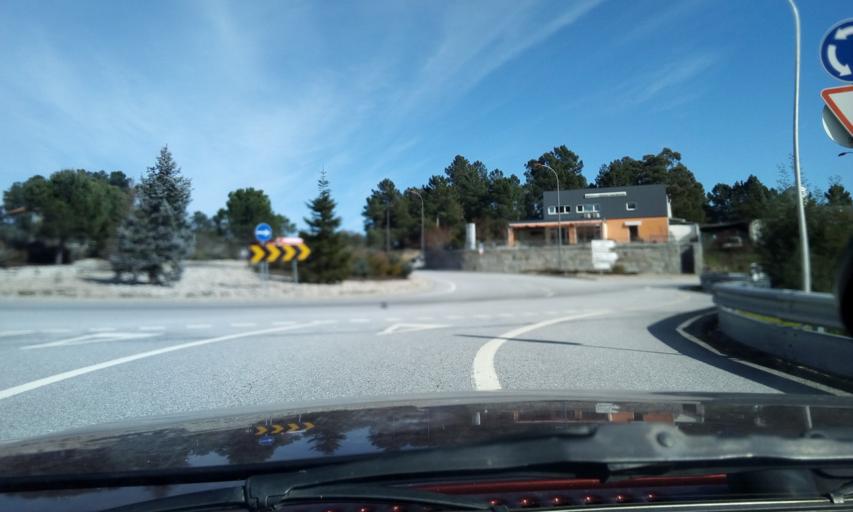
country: PT
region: Guarda
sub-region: Fornos de Algodres
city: Fornos de Algodres
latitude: 40.6140
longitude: -7.5339
